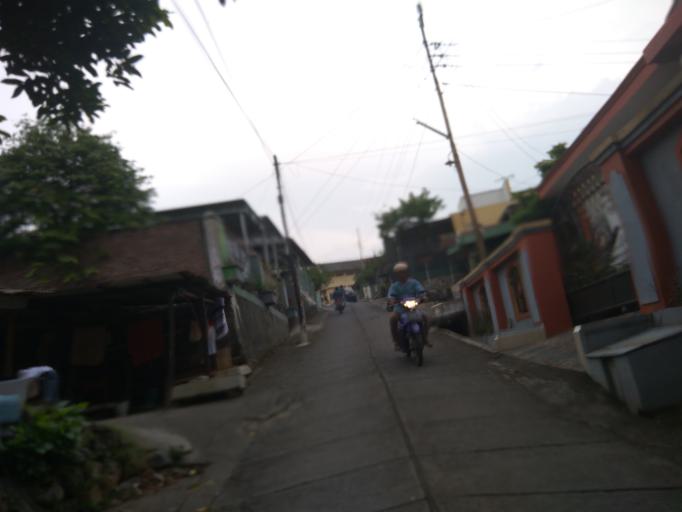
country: ID
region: Central Java
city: Semarang
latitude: -7.0099
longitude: 110.4119
